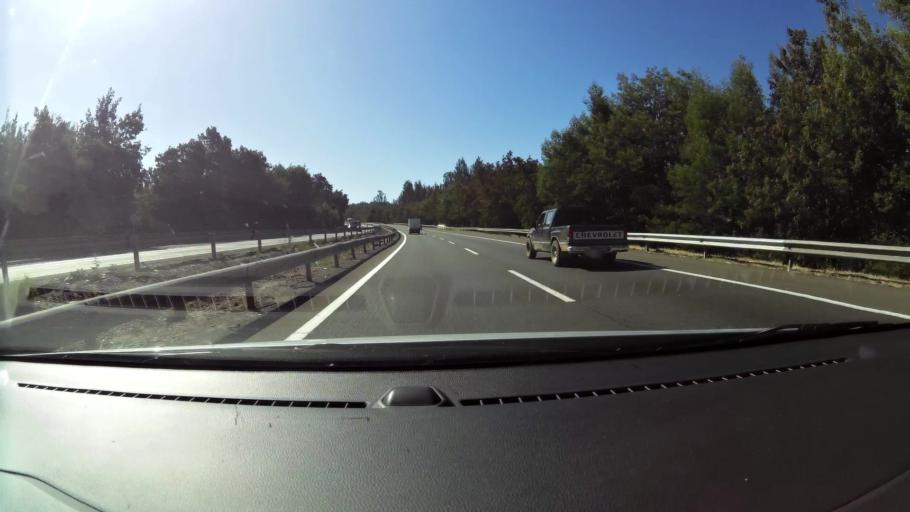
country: CL
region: Valparaiso
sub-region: Provincia de Marga Marga
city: Quilpue
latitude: -33.1796
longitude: -71.5067
